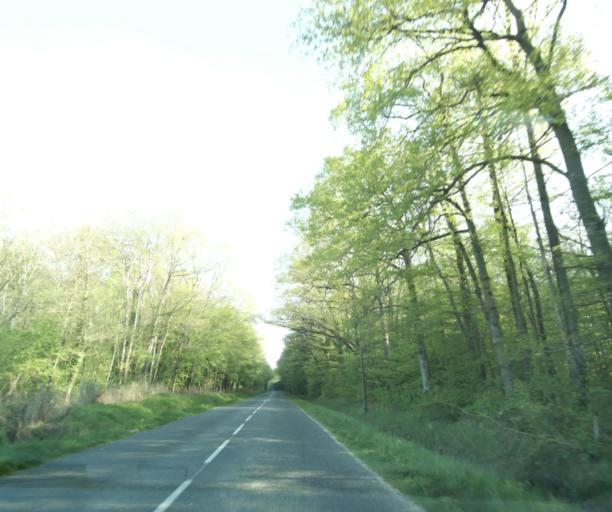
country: FR
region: Ile-de-France
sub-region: Departement de Seine-et-Marne
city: Vernou-la-Celle-sur-Seine
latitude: 48.4453
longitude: 2.8581
